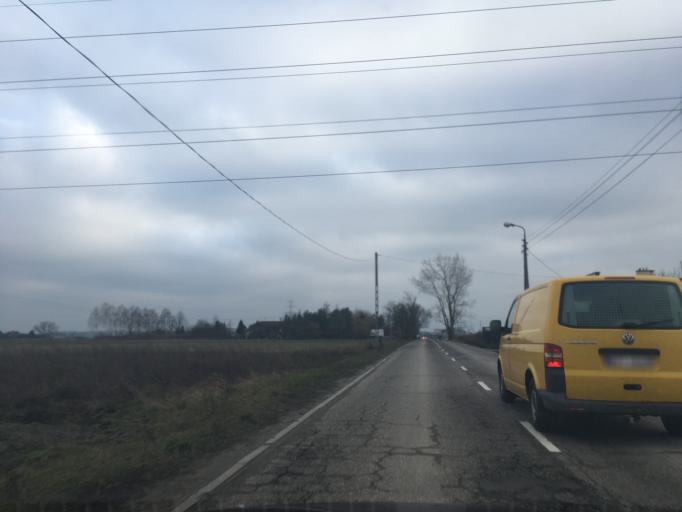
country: PL
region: Masovian Voivodeship
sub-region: Powiat piaseczynski
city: Lesznowola
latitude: 52.0897
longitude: 20.9708
